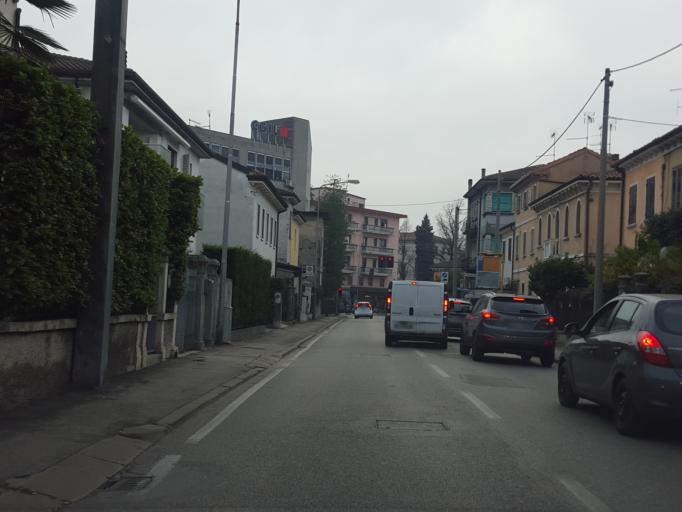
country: IT
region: Veneto
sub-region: Provincia di Vicenza
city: Vicenza
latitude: 45.5391
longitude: 11.5250
